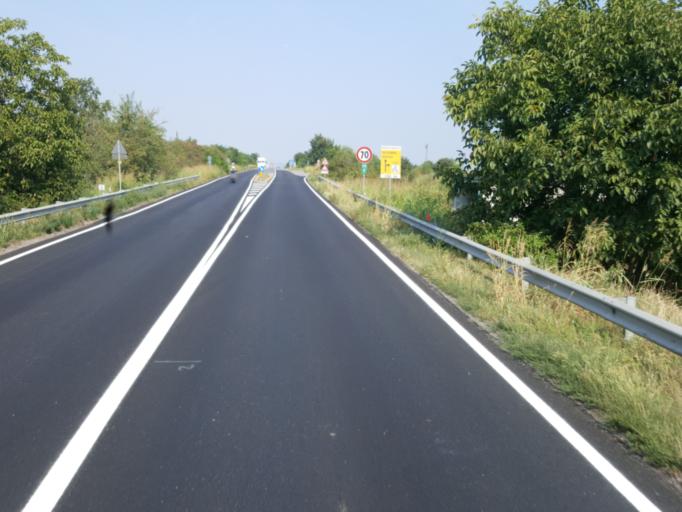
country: IT
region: Lombardy
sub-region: Provincia di Brescia
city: Travagliato
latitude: 45.4940
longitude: 10.0873
